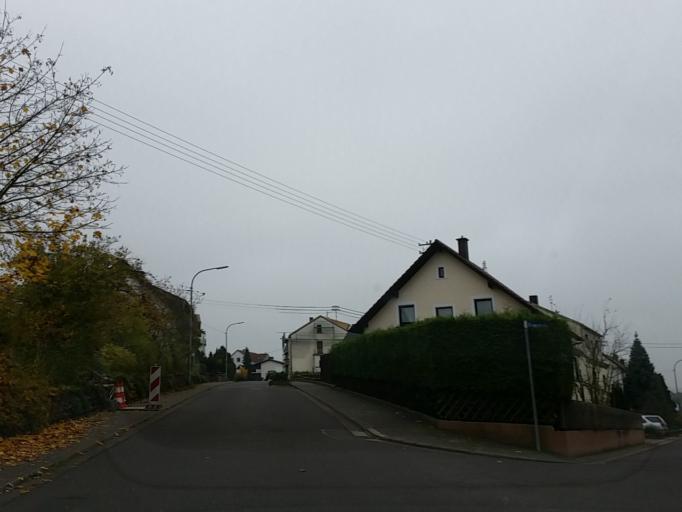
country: DE
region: Saarland
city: Schmelz
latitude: 49.4361
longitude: 6.8582
